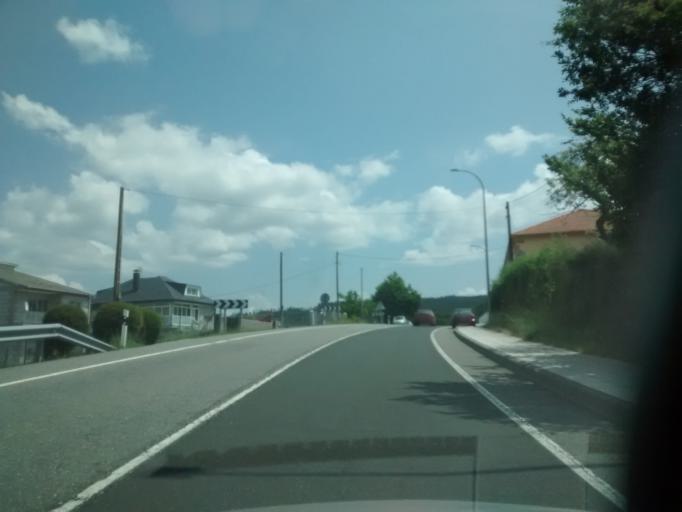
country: ES
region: Galicia
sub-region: Provincia de Pontevedra
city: Forcarei
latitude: 42.5431
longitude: -8.3556
